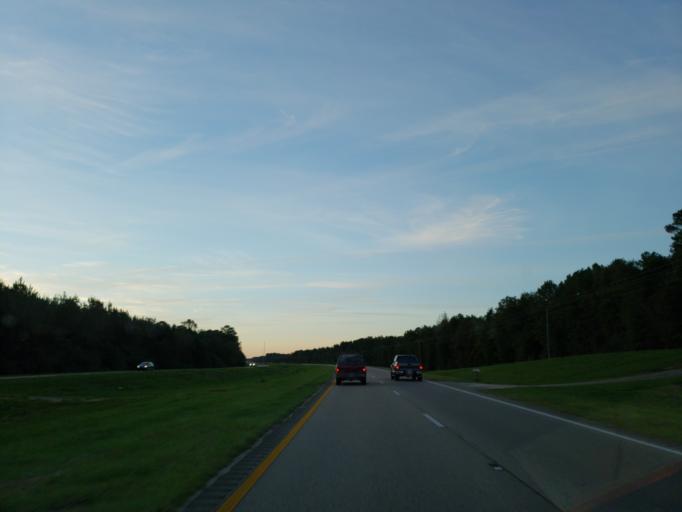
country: US
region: Mississippi
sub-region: Wayne County
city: Belmont
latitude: 31.5998
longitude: -88.5563
